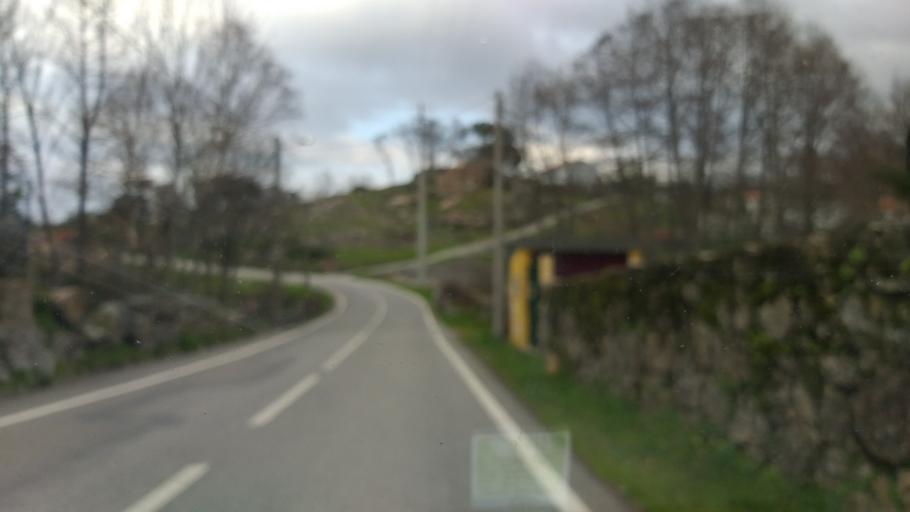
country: PT
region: Guarda
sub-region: Seia
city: Seia
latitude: 40.4843
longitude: -7.6333
